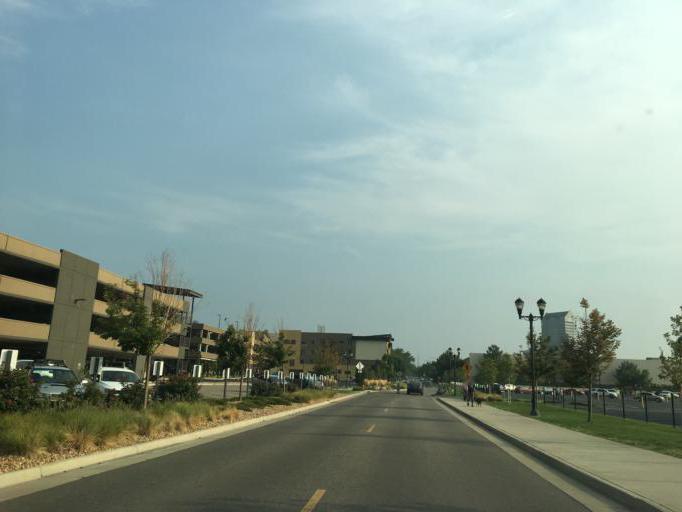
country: US
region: Colorado
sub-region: Arapahoe County
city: Glendale
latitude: 39.7041
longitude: -104.9364
